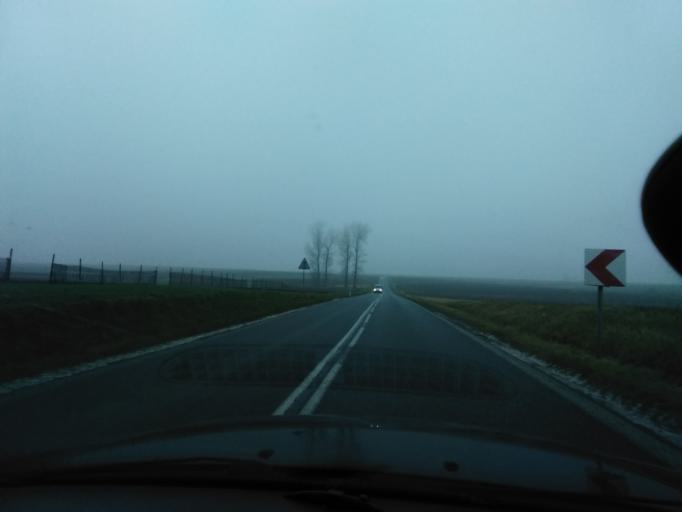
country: PL
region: Subcarpathian Voivodeship
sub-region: Powiat lancucki
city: Markowa
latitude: 50.0344
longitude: 22.3167
